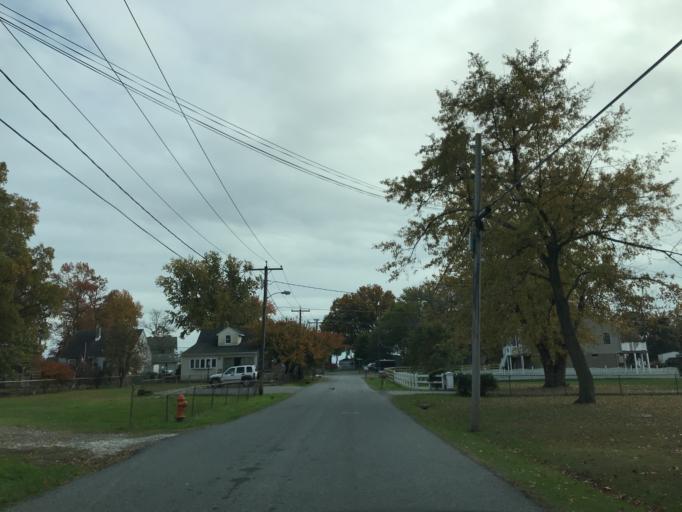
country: US
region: Maryland
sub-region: Baltimore County
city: Bowleys Quarters
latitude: 39.3076
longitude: -76.3948
